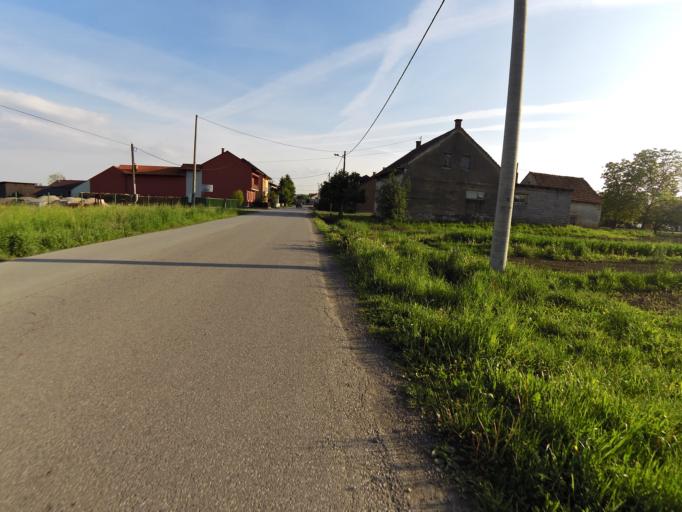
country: HR
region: Karlovacka
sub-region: Grad Karlovac
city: Karlovac
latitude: 45.5224
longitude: 15.5316
